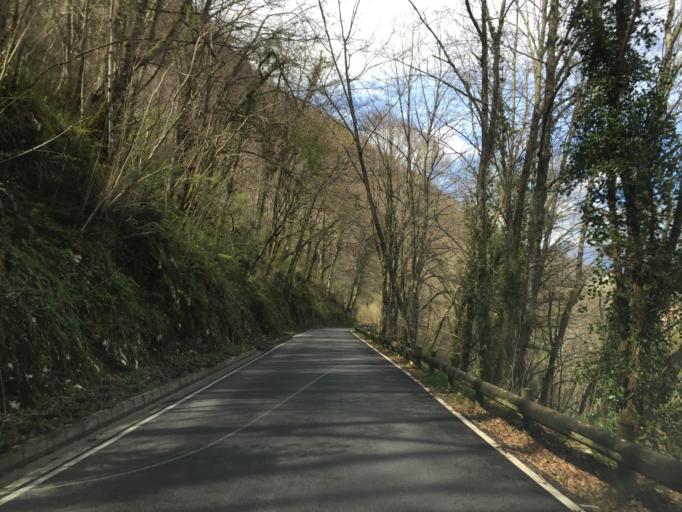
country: ES
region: Asturias
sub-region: Province of Asturias
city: Amieva
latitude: 43.3025
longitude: -5.0457
